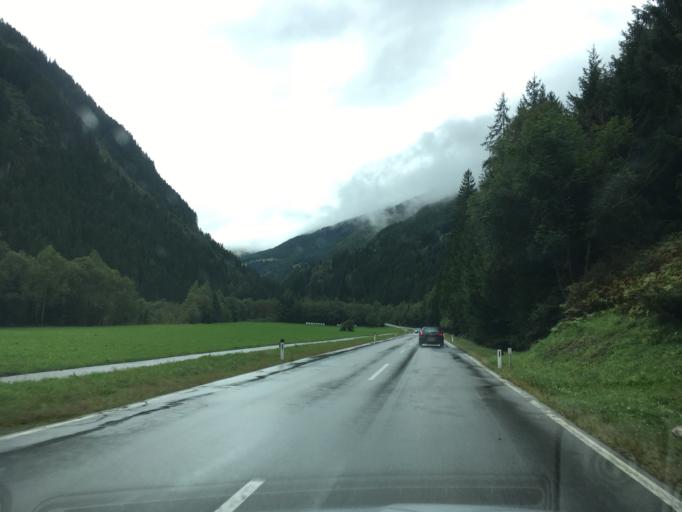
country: AT
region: Tyrol
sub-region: Politischer Bezirk Lienz
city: Hopfgarten in Defereggen
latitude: 46.9243
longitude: 12.4741
